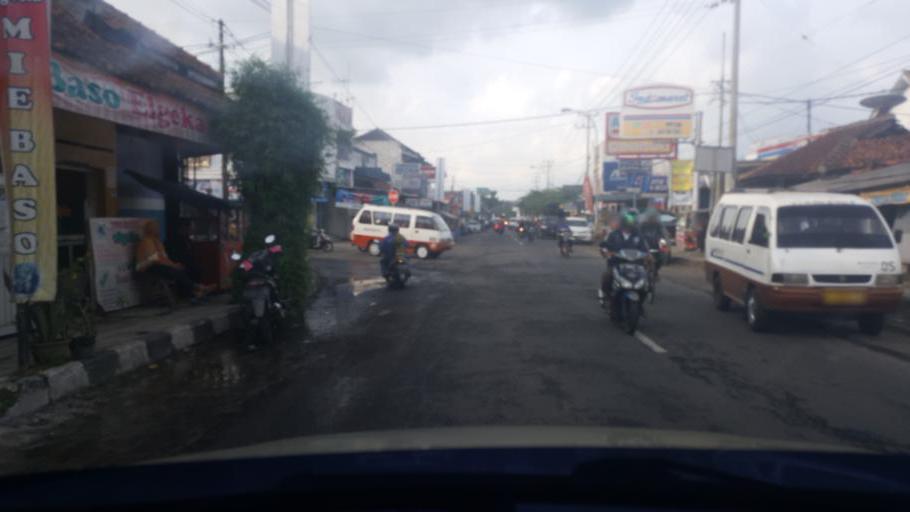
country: ID
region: West Java
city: Sindangpalay
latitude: -7.2896
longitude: 108.2004
